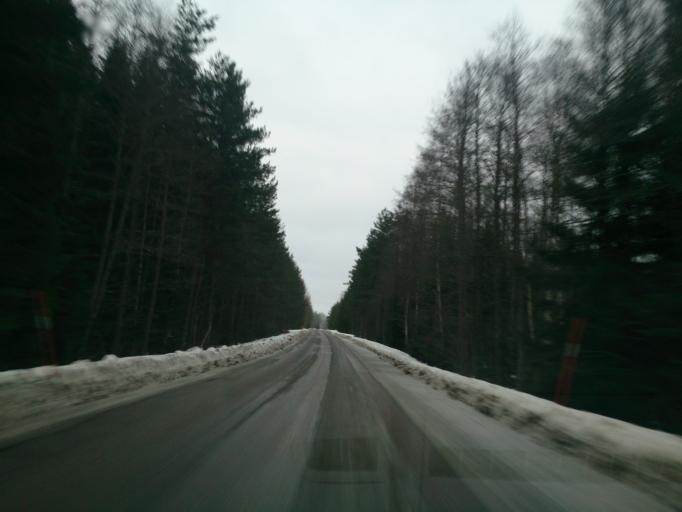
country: SE
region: OEstergoetland
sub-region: Atvidabergs Kommun
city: Atvidaberg
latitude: 58.2569
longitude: 16.0232
